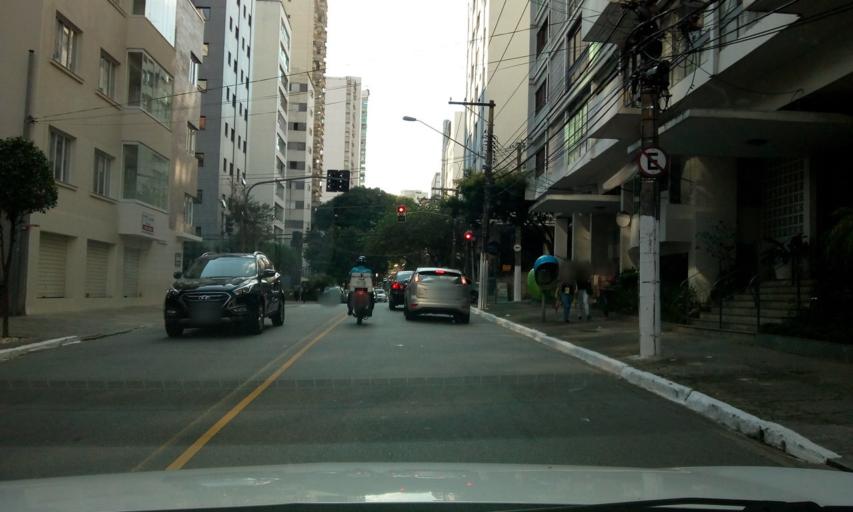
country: BR
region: Sao Paulo
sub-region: Sao Paulo
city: Sao Paulo
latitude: -23.5761
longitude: -46.6457
